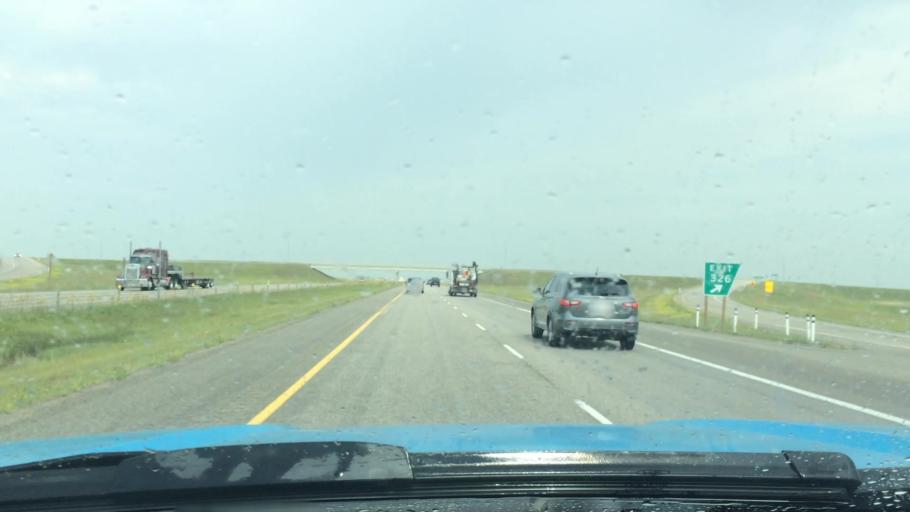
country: CA
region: Alberta
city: Didsbury
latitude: 51.6606
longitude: -114.0254
